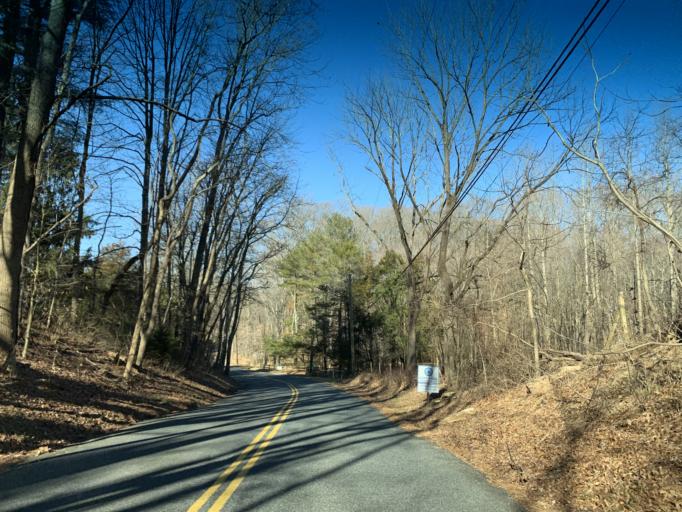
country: US
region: Maryland
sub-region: Harford County
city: South Bel Air
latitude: 39.6290
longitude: -76.2921
